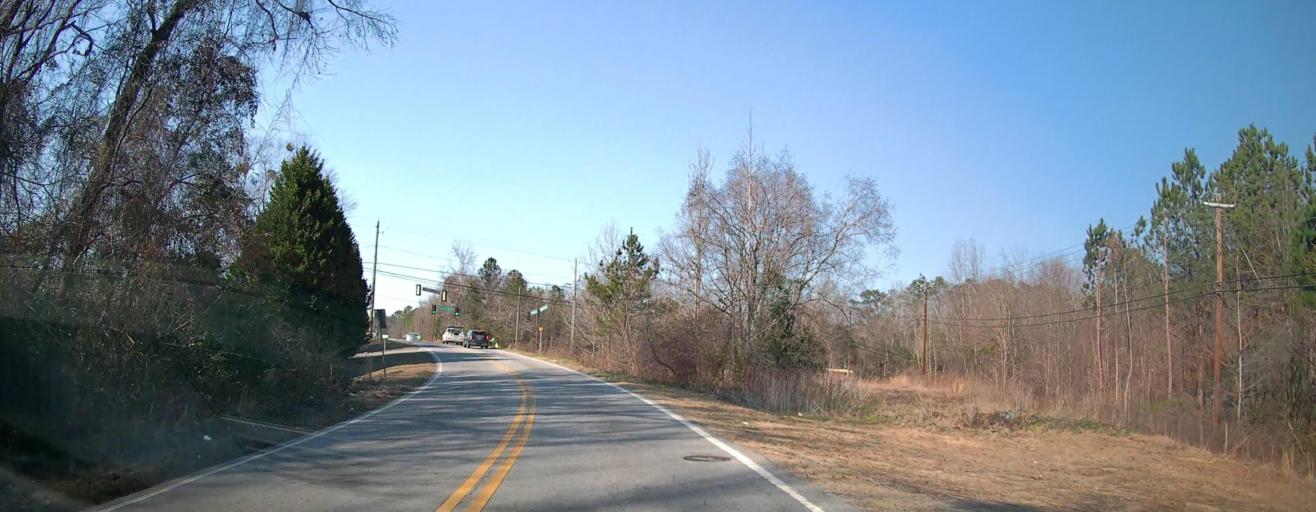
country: US
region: Georgia
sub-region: Bibb County
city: West Point
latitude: 32.8182
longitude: -83.7263
